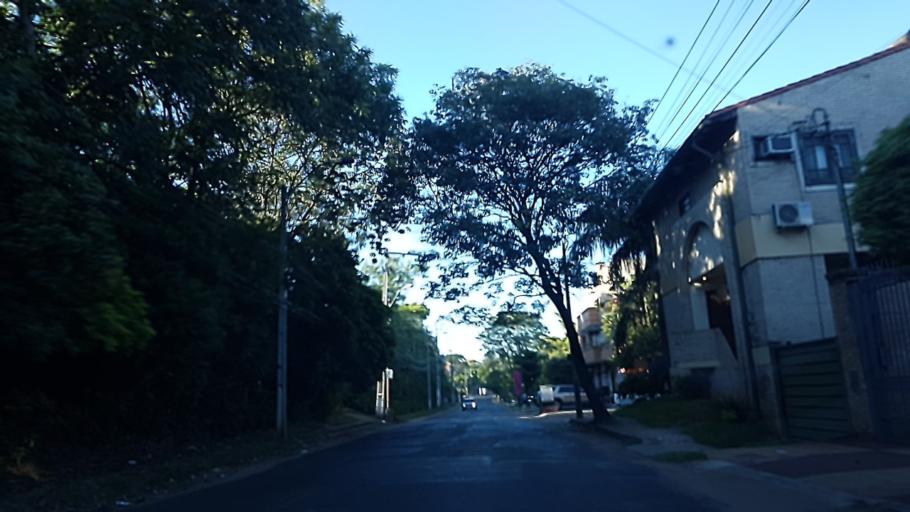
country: PY
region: Central
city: Fernando de la Mora
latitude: -25.2639
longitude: -57.5595
